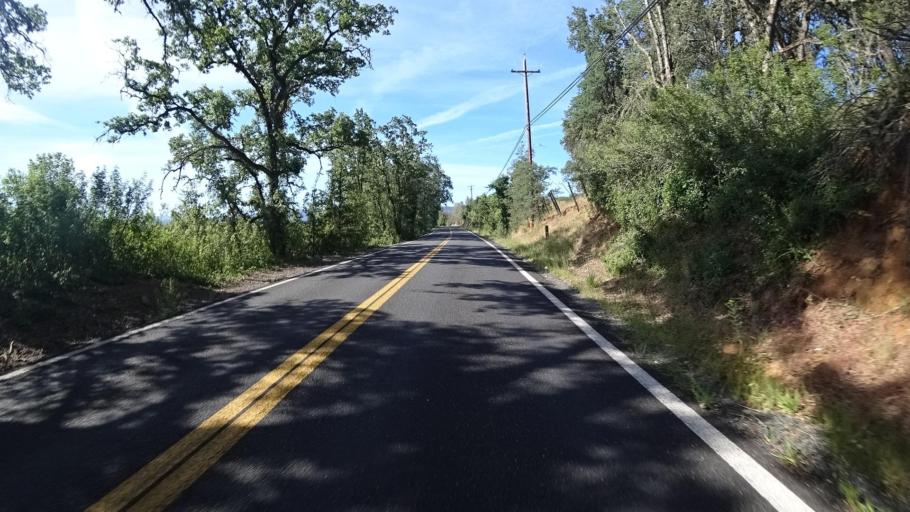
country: US
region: California
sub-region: Lake County
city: Kelseyville
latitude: 38.9659
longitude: -122.8979
